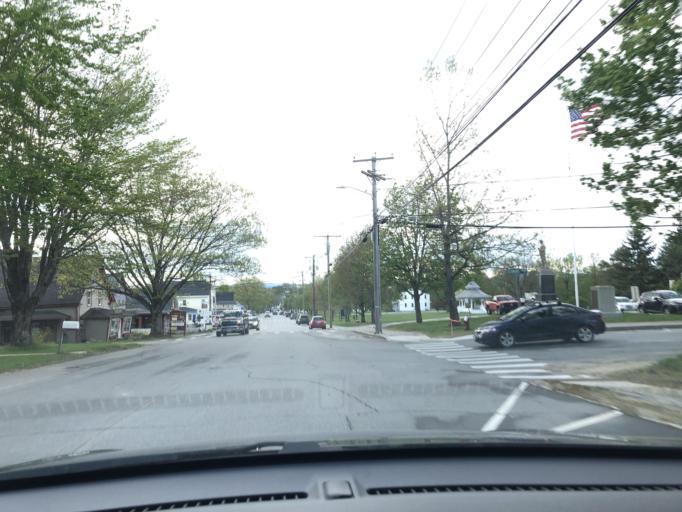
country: US
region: New Hampshire
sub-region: Merrimack County
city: New London
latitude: 43.4125
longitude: -71.9805
